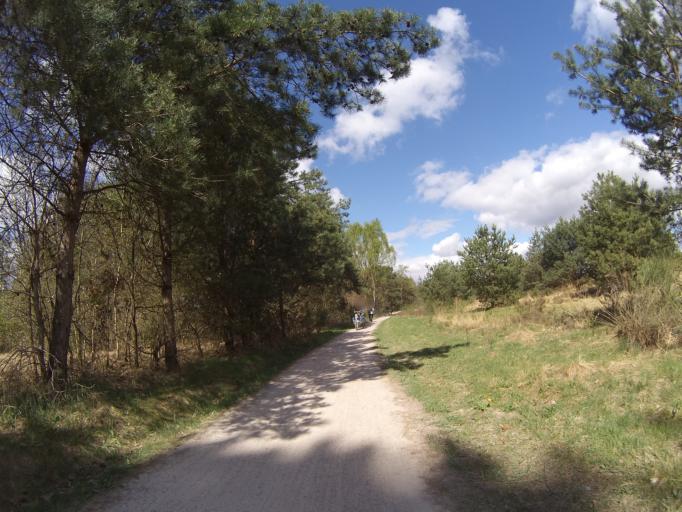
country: NL
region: North Holland
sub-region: Gemeente Bussum
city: Bussum
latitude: 52.2575
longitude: 5.1739
